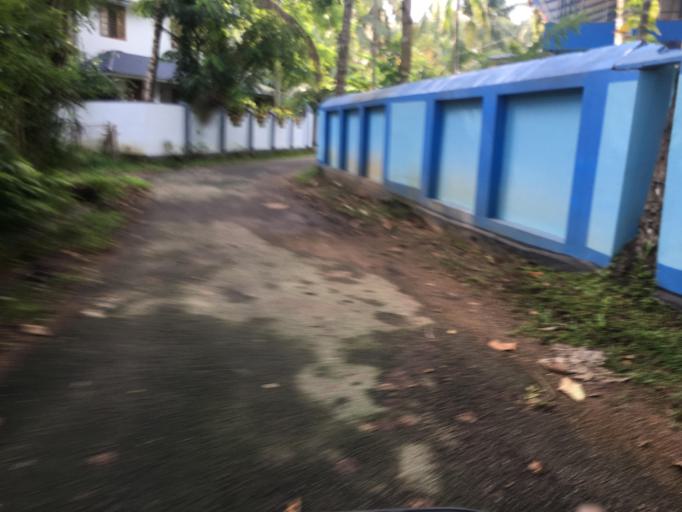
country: IN
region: Kerala
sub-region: Alappuzha
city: Kattanam
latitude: 9.1989
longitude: 76.5355
